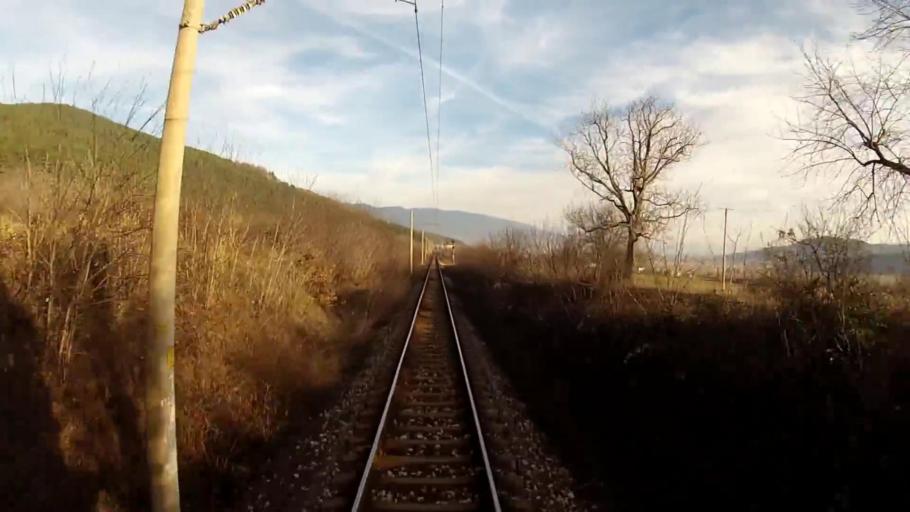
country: BG
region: Plovdiv
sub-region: Obshtina Karlovo
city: Klisura
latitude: 42.7195
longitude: 24.5838
